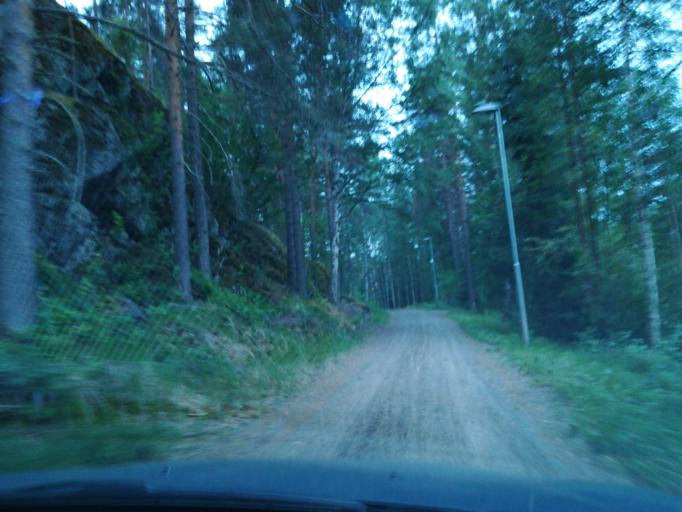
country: FI
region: Southern Savonia
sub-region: Mikkeli
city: Ristiina
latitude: 61.4970
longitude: 27.2700
